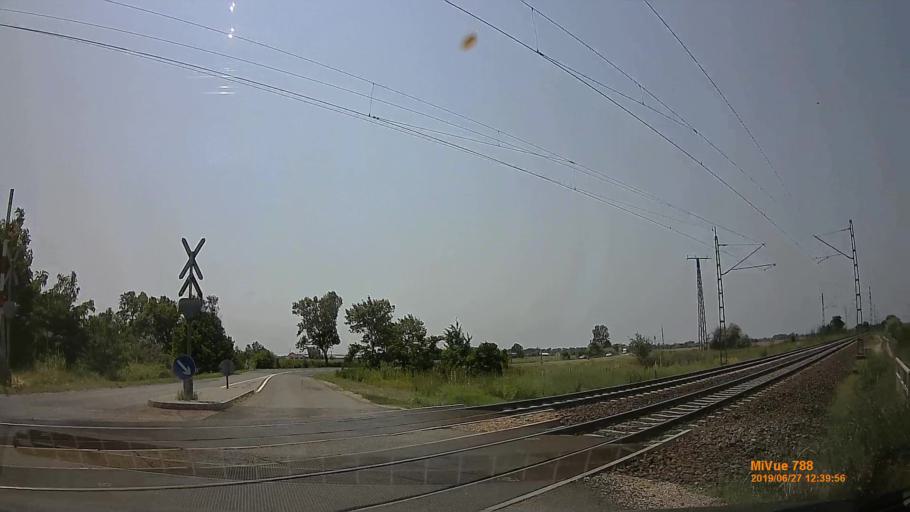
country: HU
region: Pest
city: Tortel
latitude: 47.1824
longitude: 19.9164
